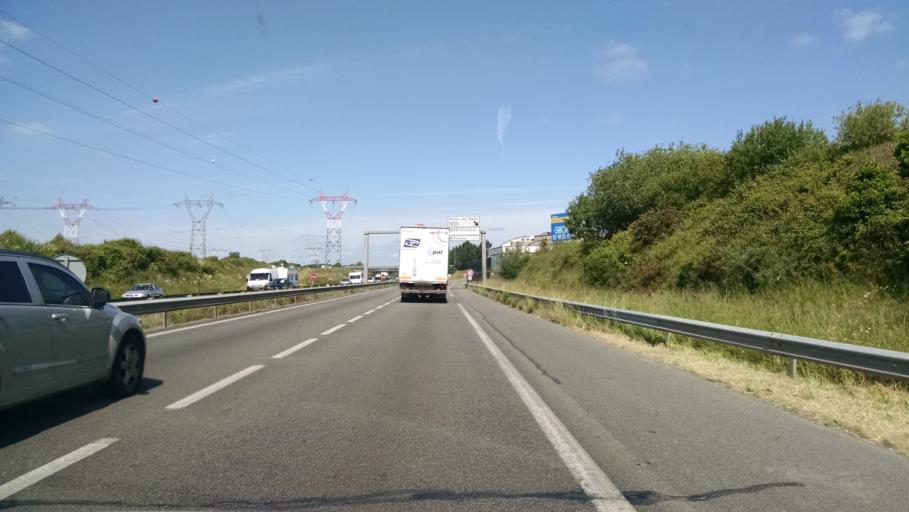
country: FR
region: Pays de la Loire
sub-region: Departement de la Loire-Atlantique
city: Reze
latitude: 47.1675
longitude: -1.5746
